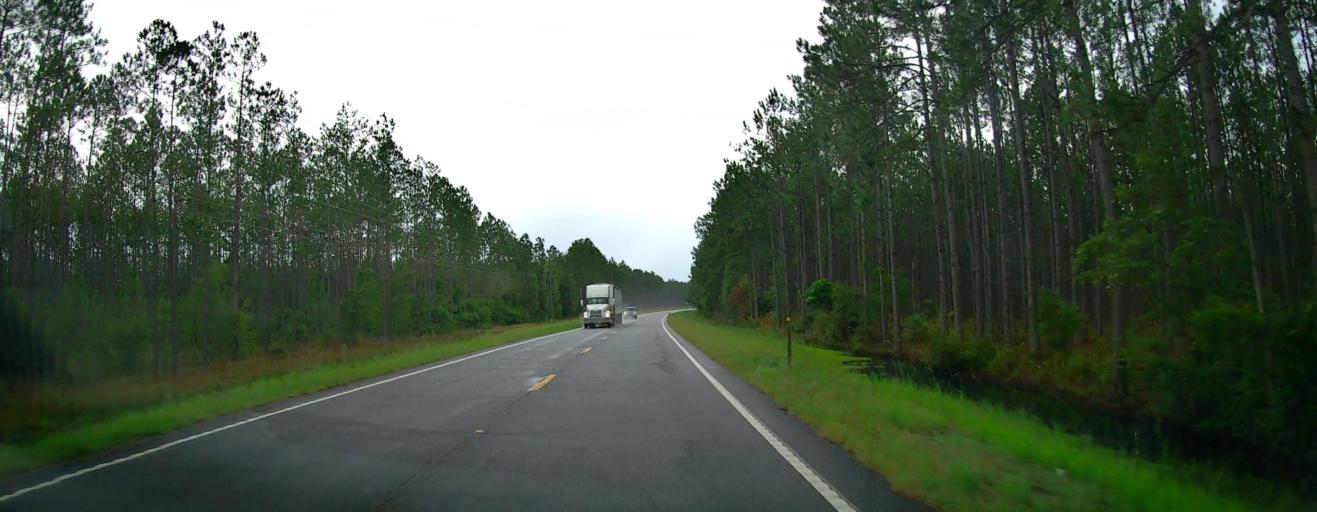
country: US
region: Georgia
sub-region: Ware County
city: Deenwood
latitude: 31.2723
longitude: -82.5273
